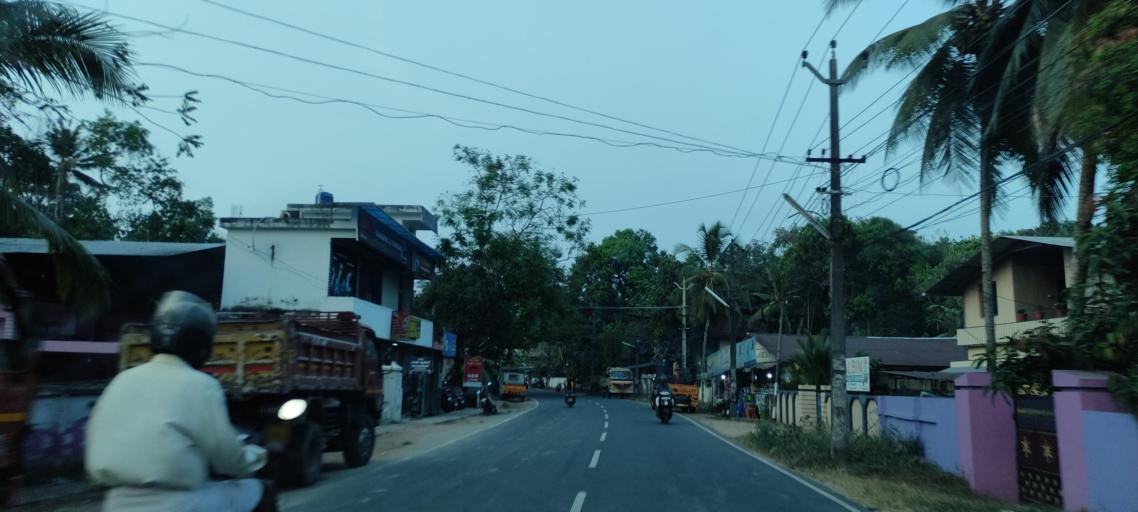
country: IN
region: Kerala
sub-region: Alappuzha
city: Mavelikara
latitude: 9.3033
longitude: 76.5341
